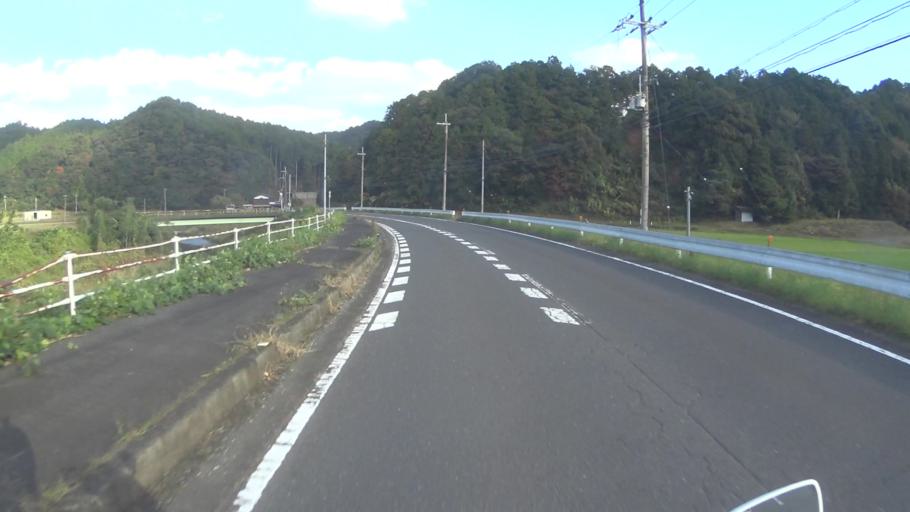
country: JP
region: Kyoto
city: Miyazu
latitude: 35.4380
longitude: 135.2192
